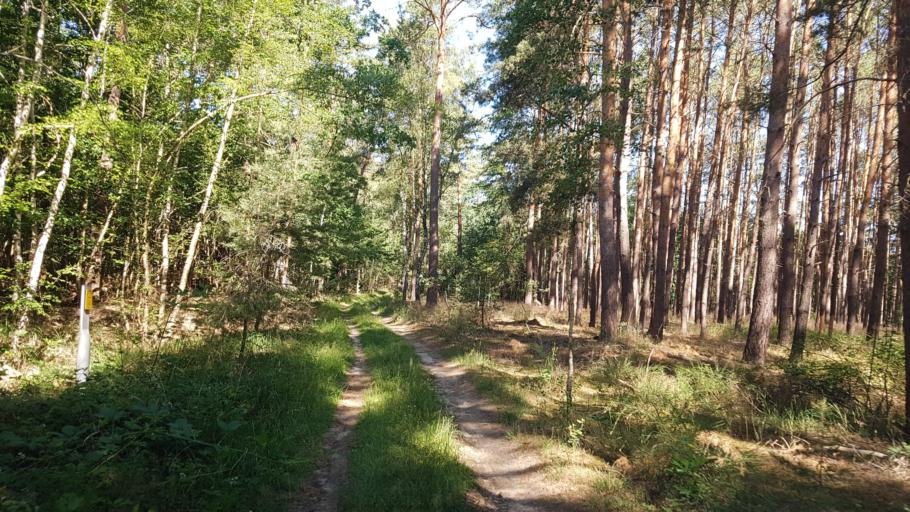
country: DE
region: Brandenburg
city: Juterbog
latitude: 51.9770
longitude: 13.1418
